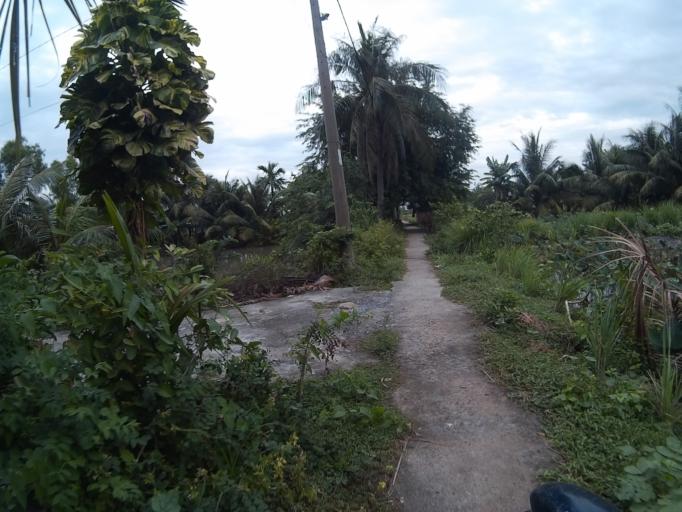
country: VN
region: Ho Chi Minh City
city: Quan Hai
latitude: 10.8124
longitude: 106.7409
